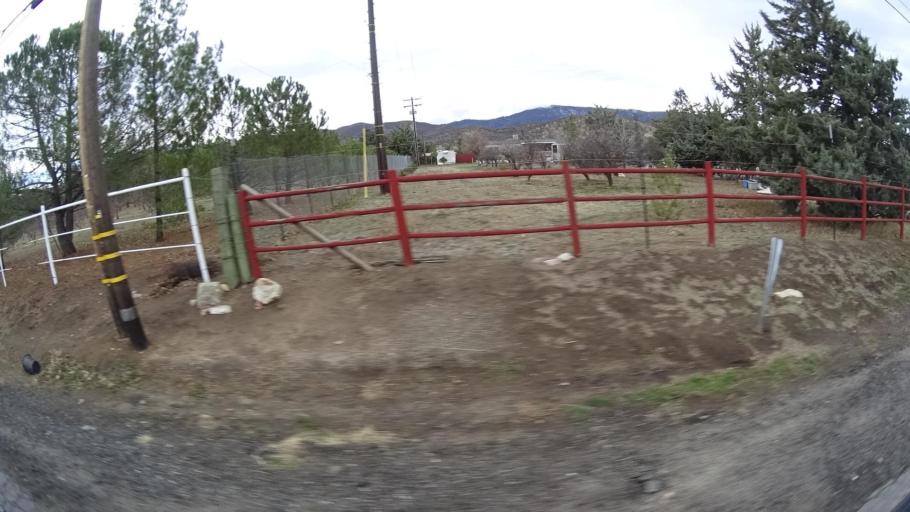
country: US
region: California
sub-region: Kern County
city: Golden Hills
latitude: 35.1168
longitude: -118.5441
